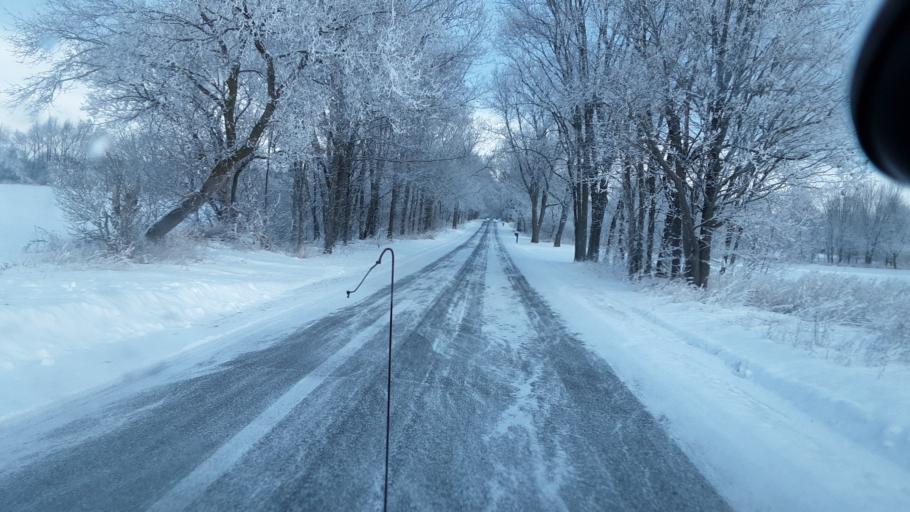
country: US
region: Michigan
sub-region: Ingham County
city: Leslie
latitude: 42.4381
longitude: -84.4970
